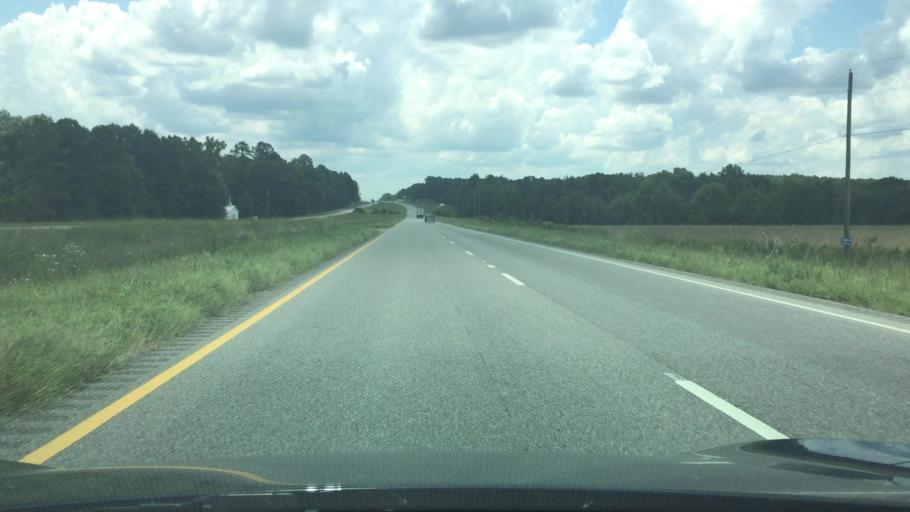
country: US
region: Alabama
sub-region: Montgomery County
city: Taylor
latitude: 32.0292
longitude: -86.0325
